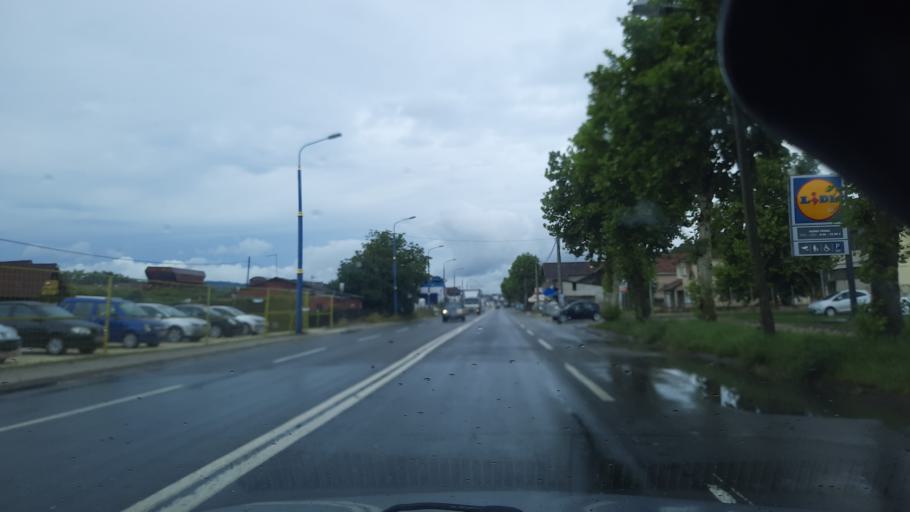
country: RS
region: Central Serbia
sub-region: Sumadijski Okrug
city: Kragujevac
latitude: 43.9972
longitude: 20.8814
